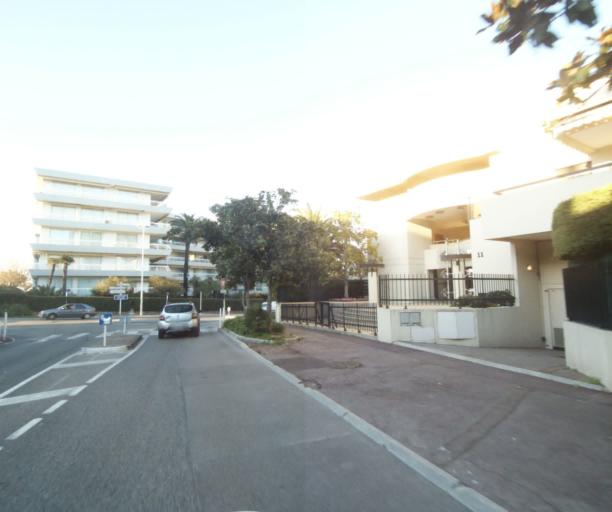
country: FR
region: Provence-Alpes-Cote d'Azur
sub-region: Departement des Alpes-Maritimes
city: Antibes
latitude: 43.5702
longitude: 7.1242
